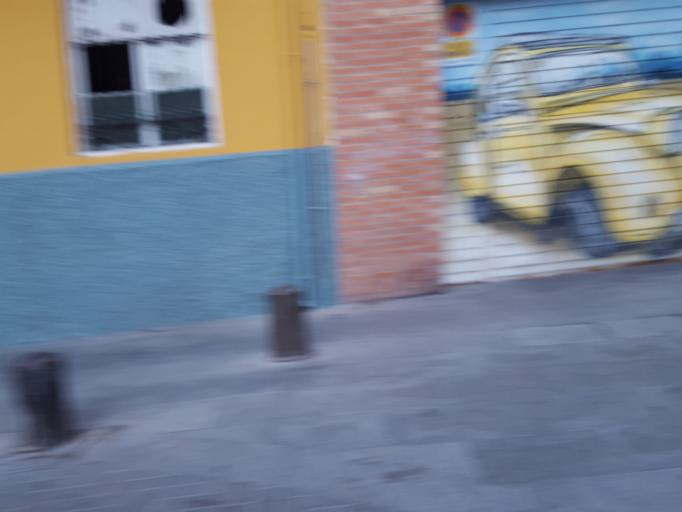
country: ES
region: Murcia
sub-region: Murcia
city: Murcia
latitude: 37.9844
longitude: -1.1364
